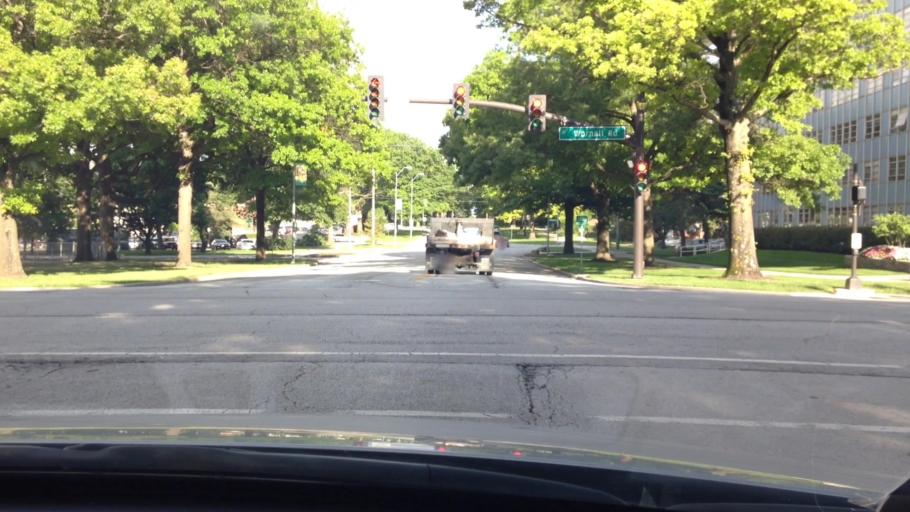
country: US
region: Kansas
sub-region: Johnson County
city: Mission Hills
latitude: 39.0123
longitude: -94.5934
